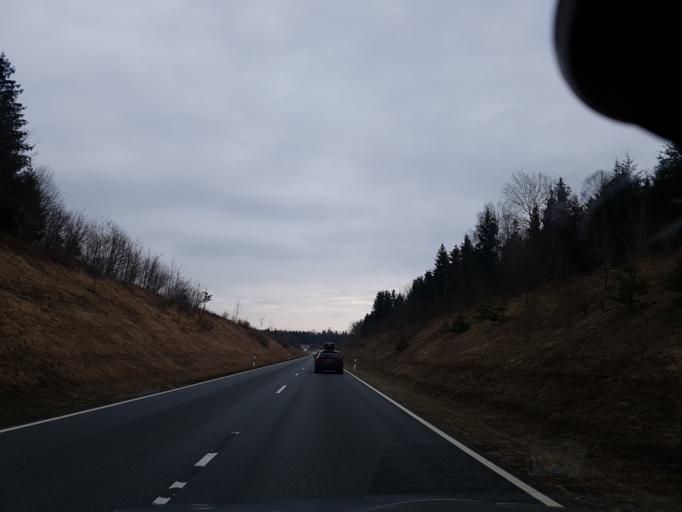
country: DE
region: Bavaria
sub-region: Upper Bavaria
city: Brunnthal
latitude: 48.0170
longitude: 11.6963
